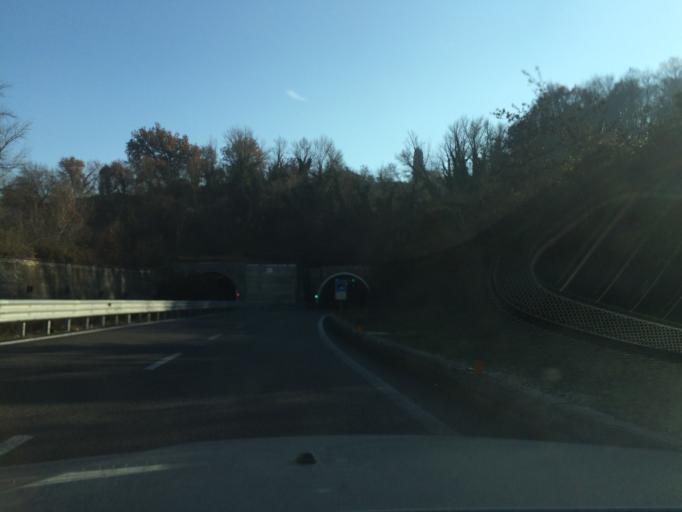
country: IT
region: Umbria
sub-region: Provincia di Perugia
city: Massa Martana
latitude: 42.7479
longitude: 12.4701
